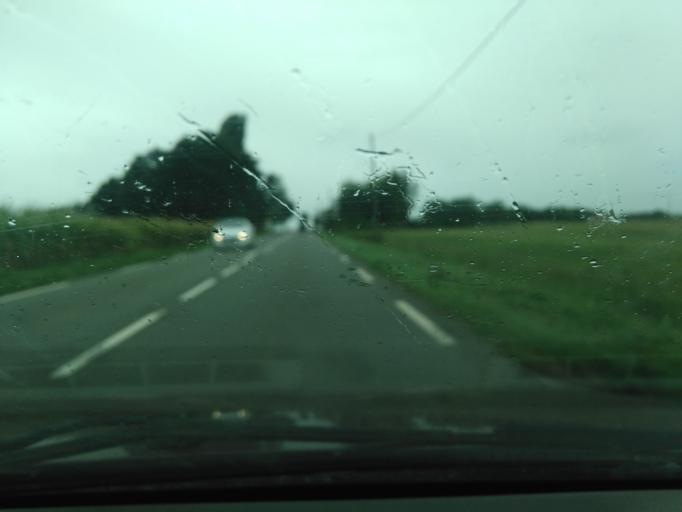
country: FR
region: Pays de la Loire
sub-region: Departement de la Vendee
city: Sainte-Hermine
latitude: 46.5701
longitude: -1.0882
